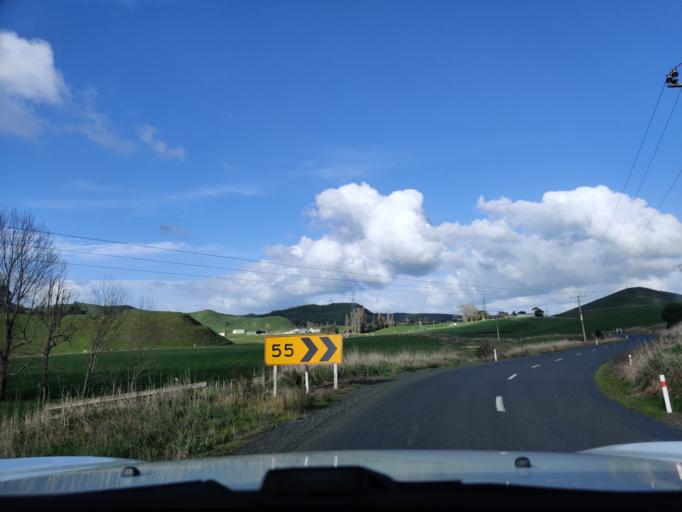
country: NZ
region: Waikato
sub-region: Waikato District
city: Te Kauwhata
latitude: -37.2843
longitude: 175.2111
